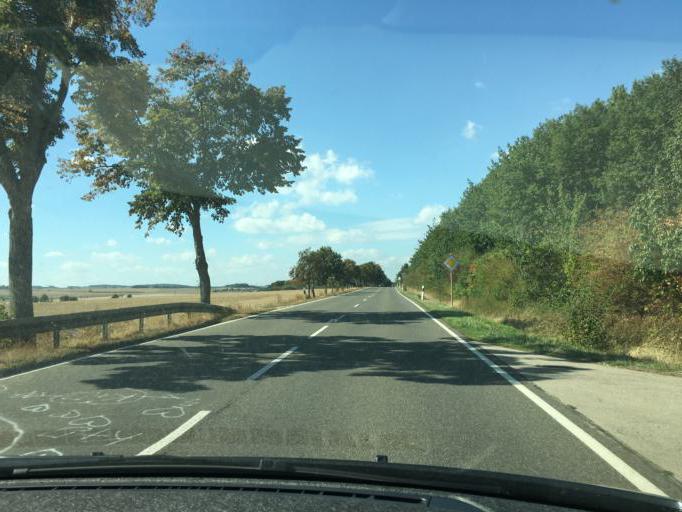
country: DE
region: North Rhine-Westphalia
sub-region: Regierungsbezirk Koln
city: Vettweiss
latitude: 50.6703
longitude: 6.5955
